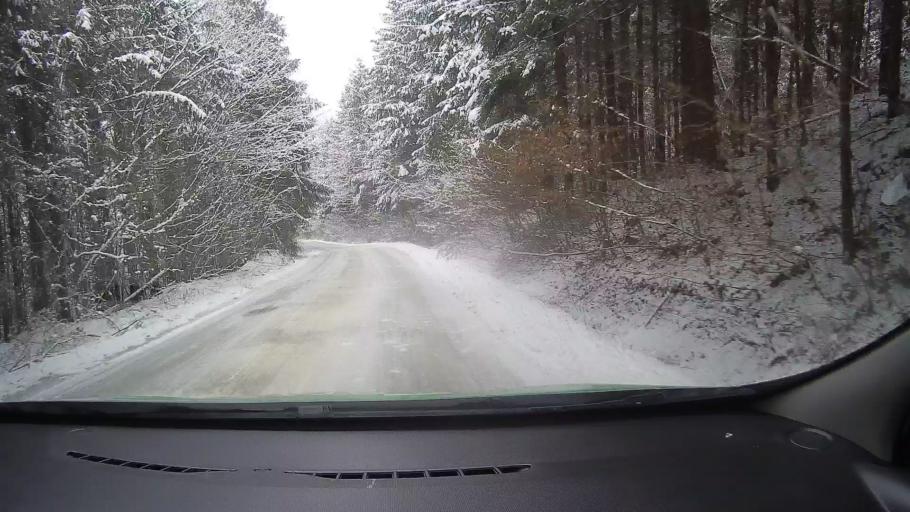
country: RO
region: Alba
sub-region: Comuna Almasu Mare
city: Almasu Mare
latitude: 46.0978
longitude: 23.1477
